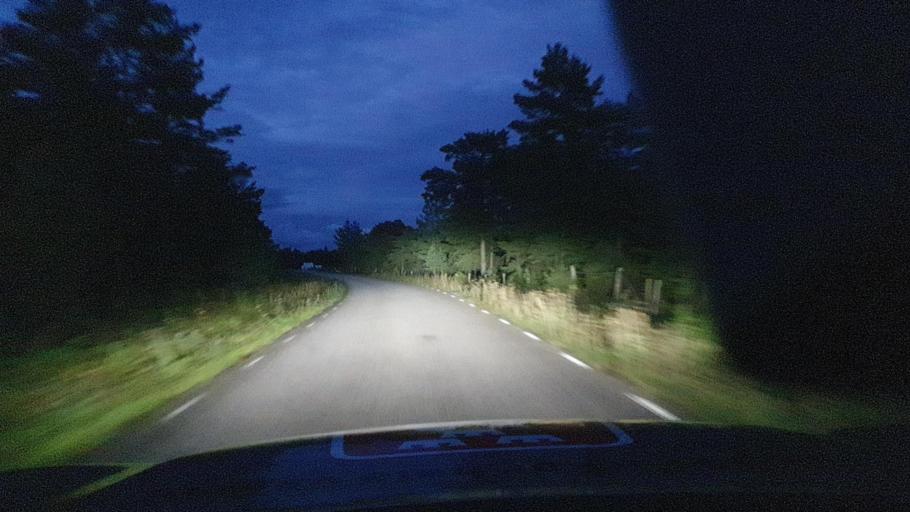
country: SE
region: Gotland
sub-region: Gotland
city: Slite
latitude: 57.8247
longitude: 18.6565
